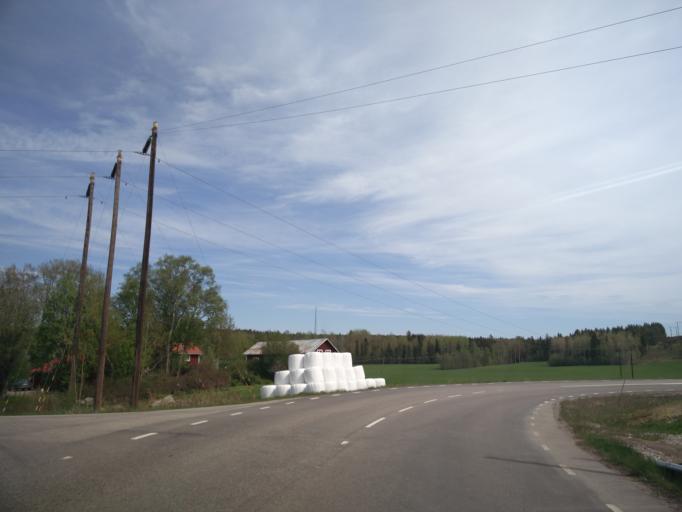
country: SE
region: Gaevleborg
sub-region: Hudiksvalls Kommun
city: Sorforsa
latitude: 61.7240
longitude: 16.9842
